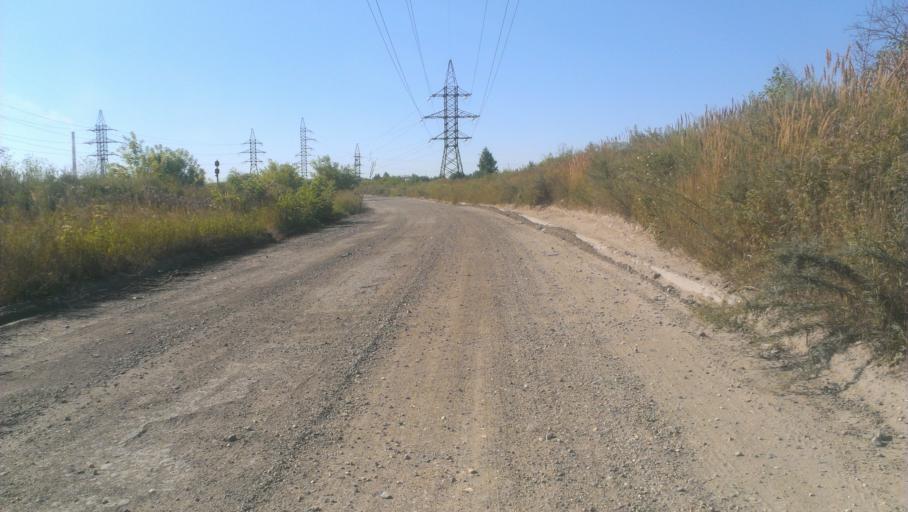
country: RU
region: Altai Krai
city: Novosilikatnyy
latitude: 53.3263
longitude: 83.6482
